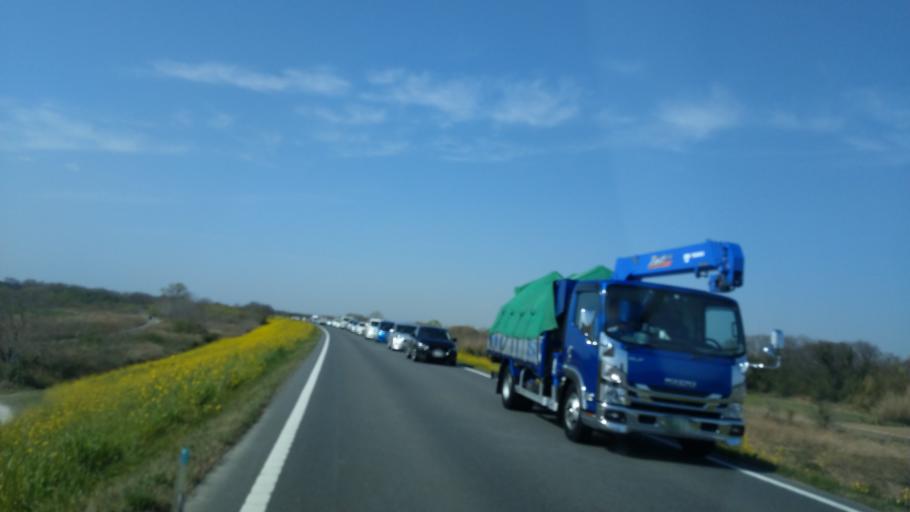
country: JP
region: Saitama
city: Okegawa
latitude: 35.9438
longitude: 139.5361
